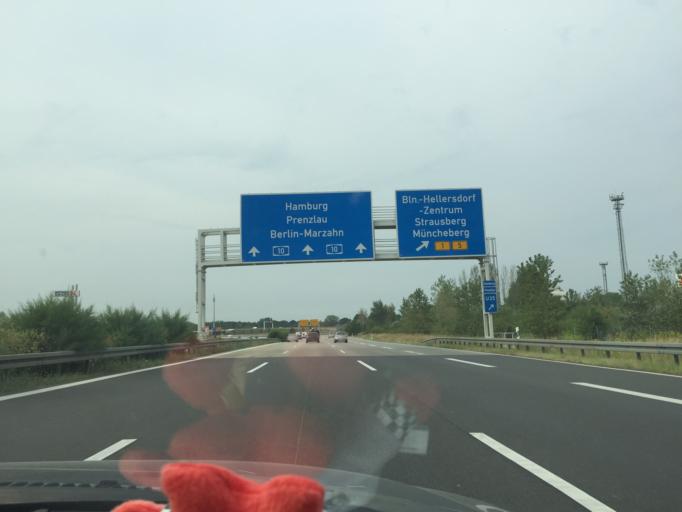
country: DE
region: Brandenburg
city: Woltersdorf
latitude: 52.4918
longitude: 13.7536
